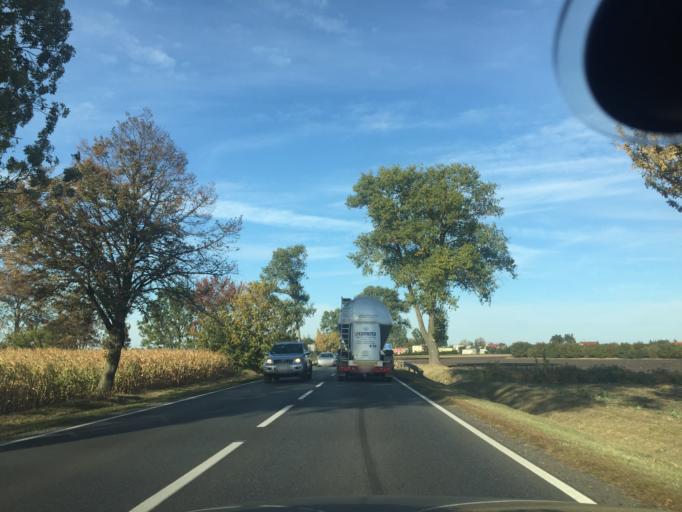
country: PL
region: Kujawsko-Pomorskie
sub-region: Powiat inowroclawski
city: Inowroclaw
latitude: 52.7270
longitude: 18.2311
